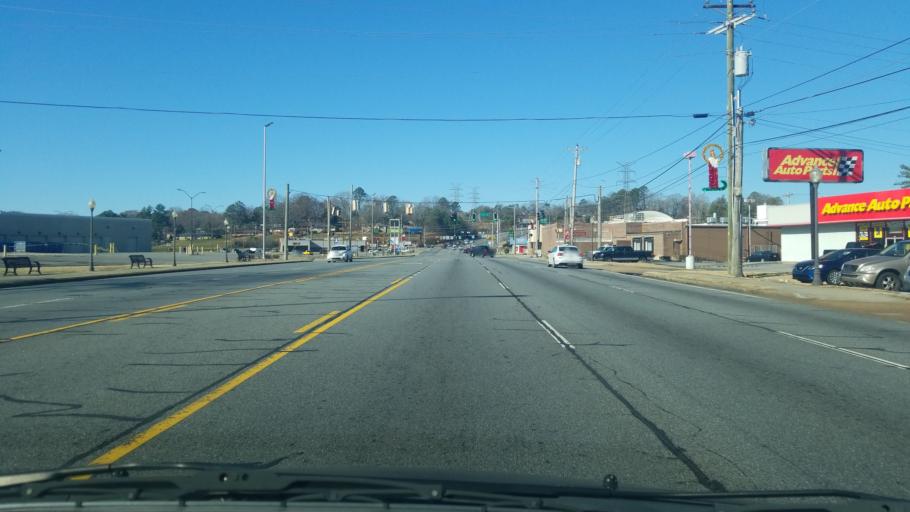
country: US
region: Georgia
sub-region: Catoosa County
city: Fort Oglethorpe
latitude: 34.9546
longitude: -85.2549
